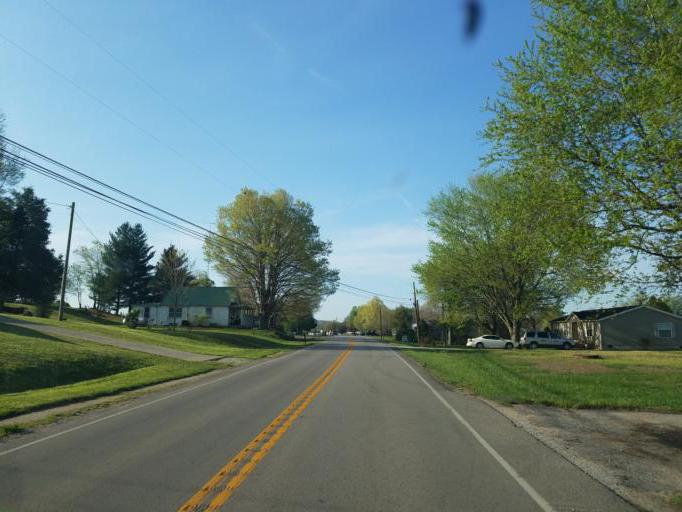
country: US
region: Kentucky
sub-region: Hart County
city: Munfordville
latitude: 37.3903
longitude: -85.9037
